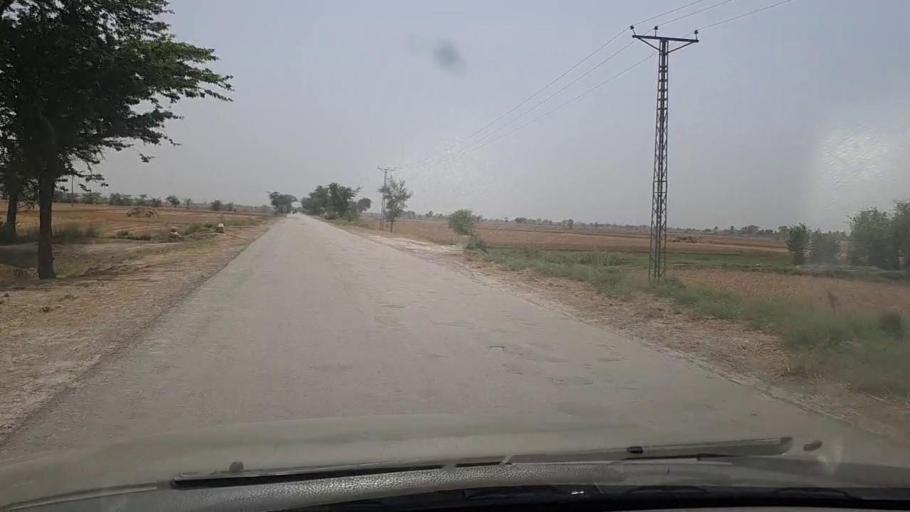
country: PK
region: Sindh
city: Miro Khan
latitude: 27.7030
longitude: 68.0618
